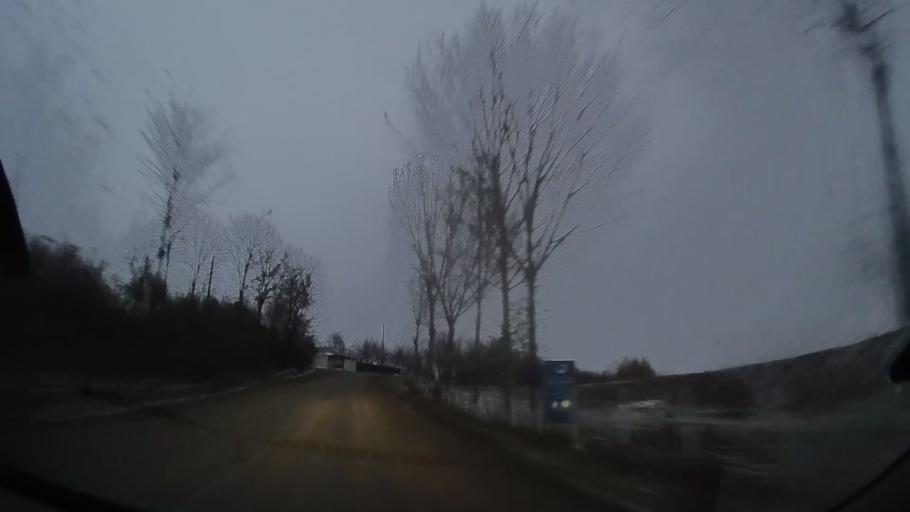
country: RO
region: Vaslui
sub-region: Comuna Vutcani
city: Vutcani
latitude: 46.4173
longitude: 27.9976
